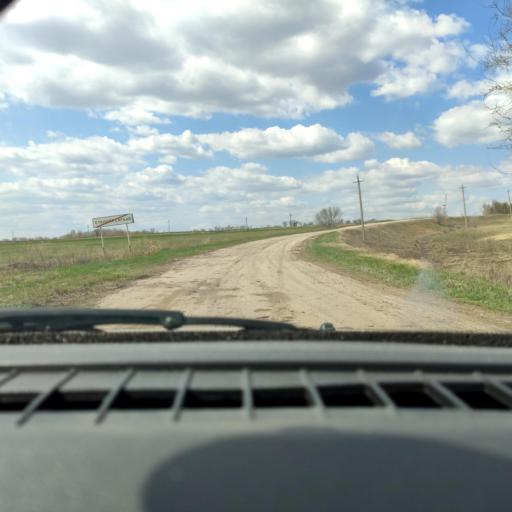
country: RU
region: Samara
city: Krotovka
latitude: 53.5343
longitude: 51.1384
